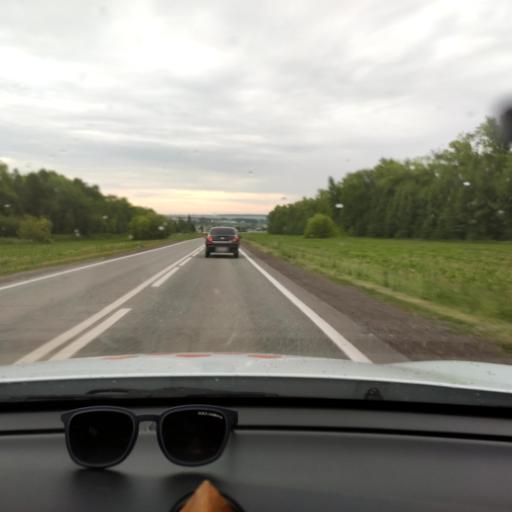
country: RU
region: Tatarstan
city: Pestretsy
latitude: 55.8356
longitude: 49.6519
